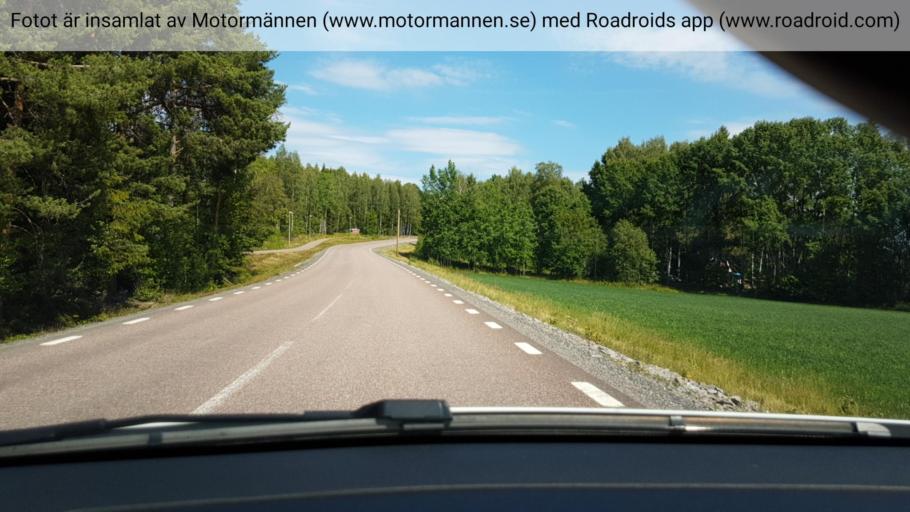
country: SE
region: Dalarna
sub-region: Borlange Kommun
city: Ornas
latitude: 60.5962
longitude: 15.5216
